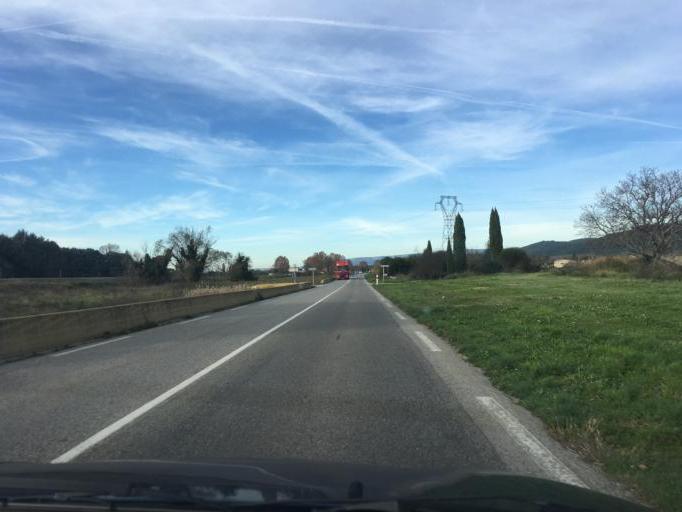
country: FR
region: Provence-Alpes-Cote d'Azur
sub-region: Departement du Vaucluse
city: Villelaure
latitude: 43.7041
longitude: 5.4386
